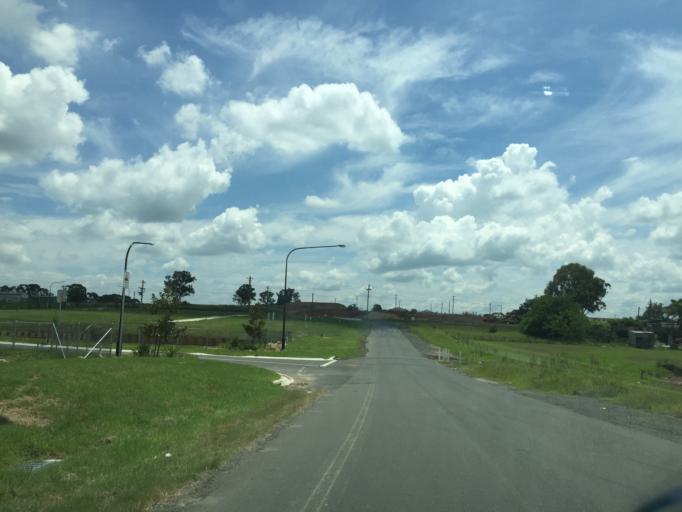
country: AU
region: New South Wales
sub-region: Blacktown
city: Riverstone
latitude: -33.6990
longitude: 150.8876
